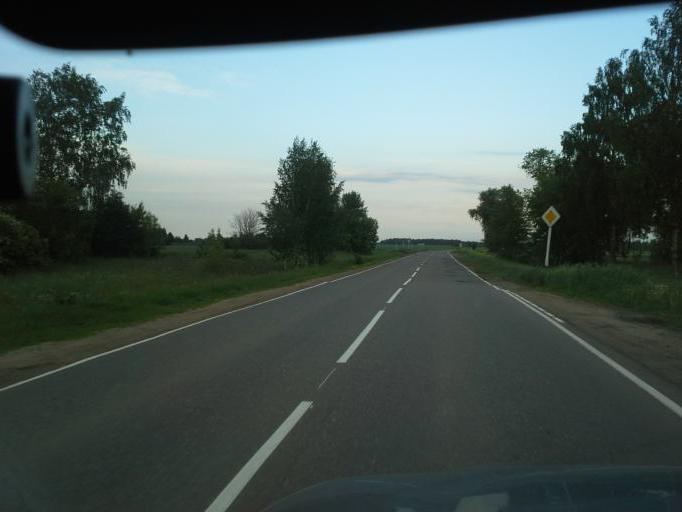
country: RU
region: Ivanovo
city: Gavrilov Posad
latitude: 56.5481
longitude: 40.1829
